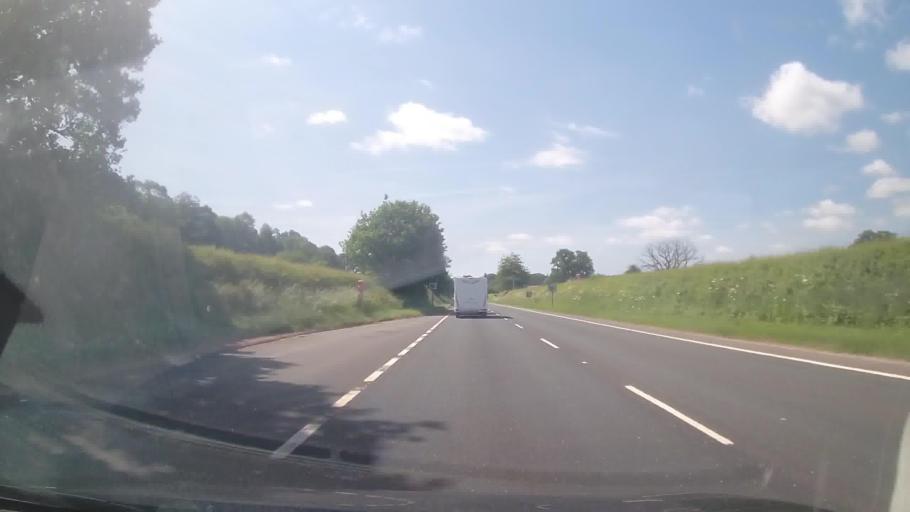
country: GB
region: England
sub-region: Shropshire
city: Ludlow
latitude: 52.3464
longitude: -2.7083
